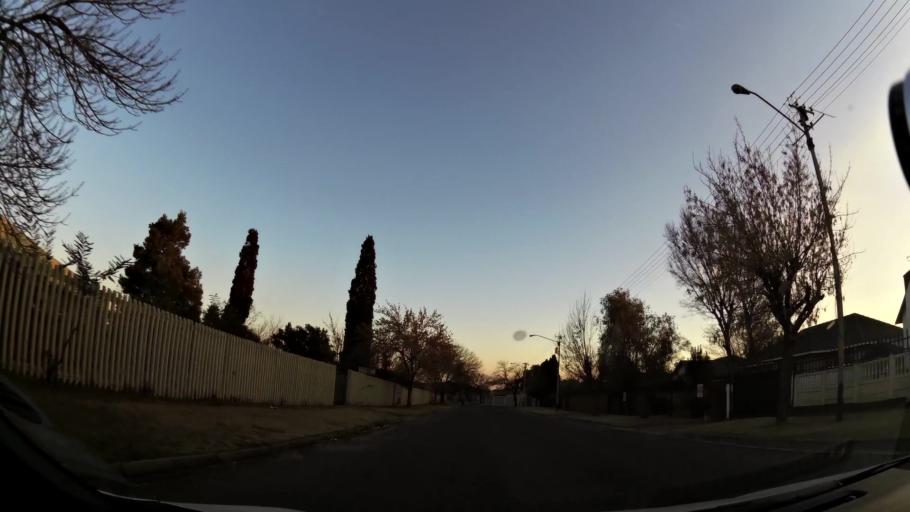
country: ZA
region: Gauteng
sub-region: Ekurhuleni Metropolitan Municipality
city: Germiston
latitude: -26.2710
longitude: 28.1574
